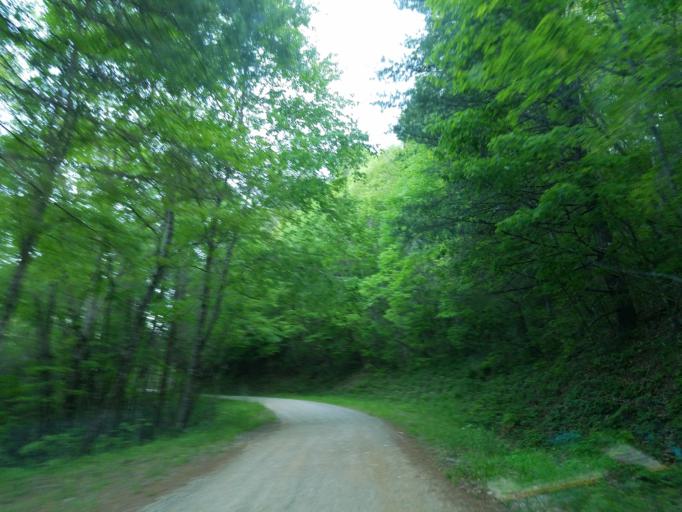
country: US
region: Georgia
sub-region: Union County
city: Blairsville
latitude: 34.7629
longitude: -84.0051
